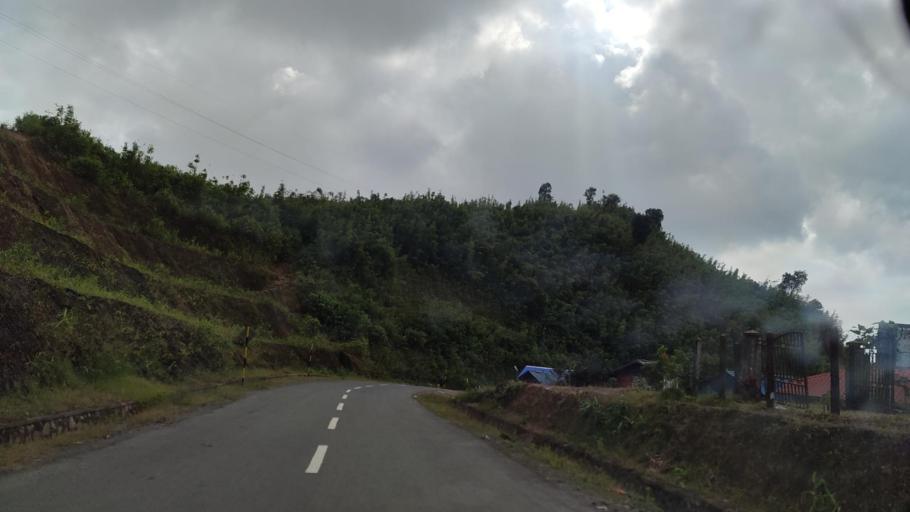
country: MM
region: Magway
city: Minbu
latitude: 19.8231
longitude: 94.2781
